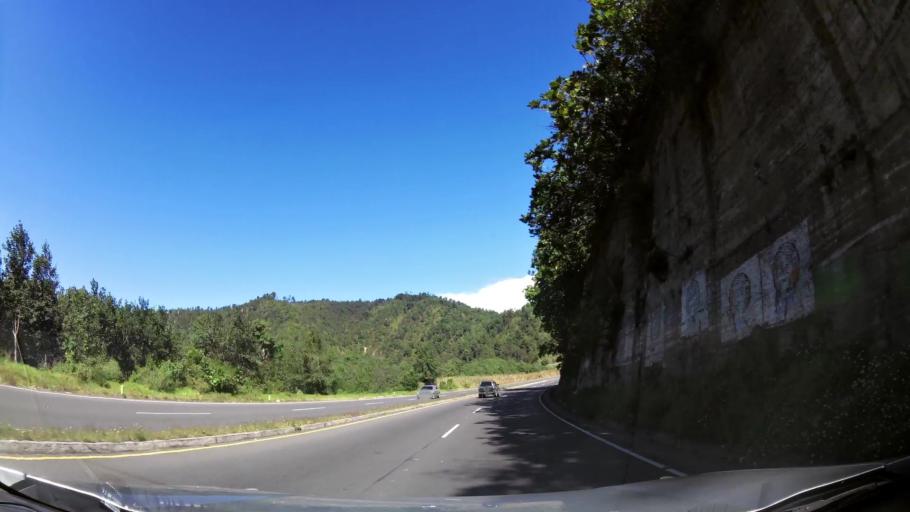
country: GT
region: Solola
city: Solola
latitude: 14.8177
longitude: -91.2018
